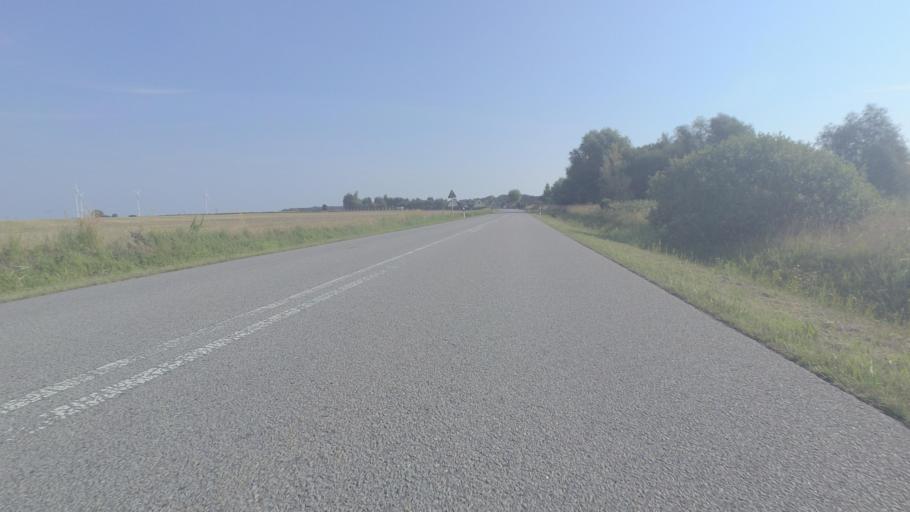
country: DE
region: Mecklenburg-Vorpommern
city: Grimmen
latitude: 54.1311
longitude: 13.0521
